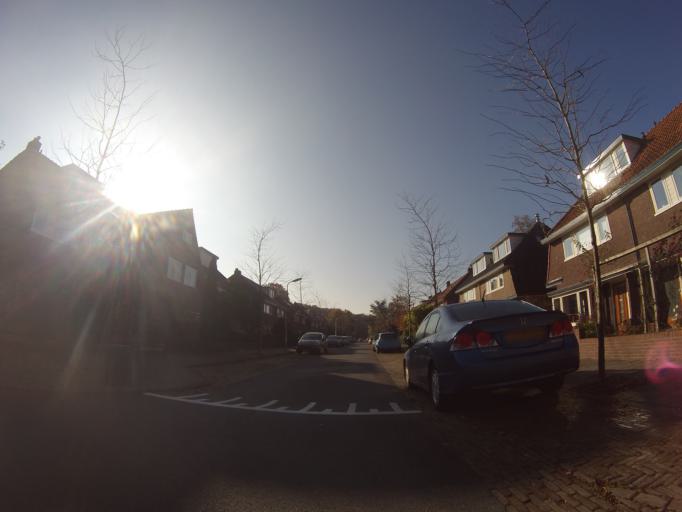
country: NL
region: Utrecht
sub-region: Gemeente Amersfoort
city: Amersfoort
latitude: 52.1417
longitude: 5.3856
